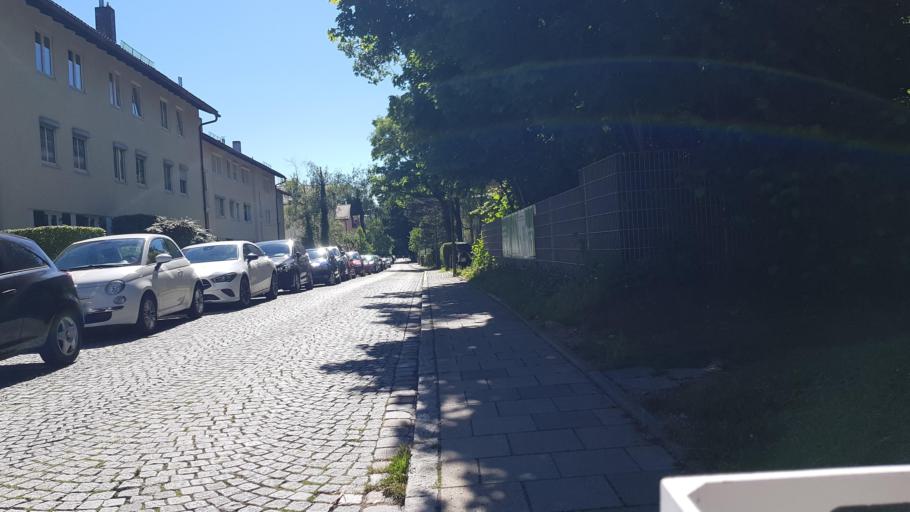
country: DE
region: Bavaria
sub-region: Upper Bavaria
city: Munich
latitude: 48.1142
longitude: 11.6067
